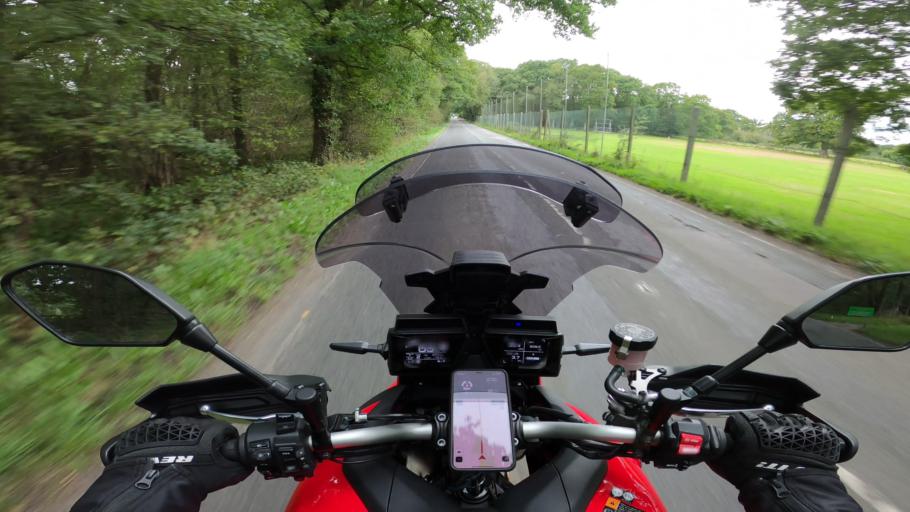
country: GB
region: England
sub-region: Surrey
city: Felbridge
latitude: 51.1616
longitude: -0.0583
